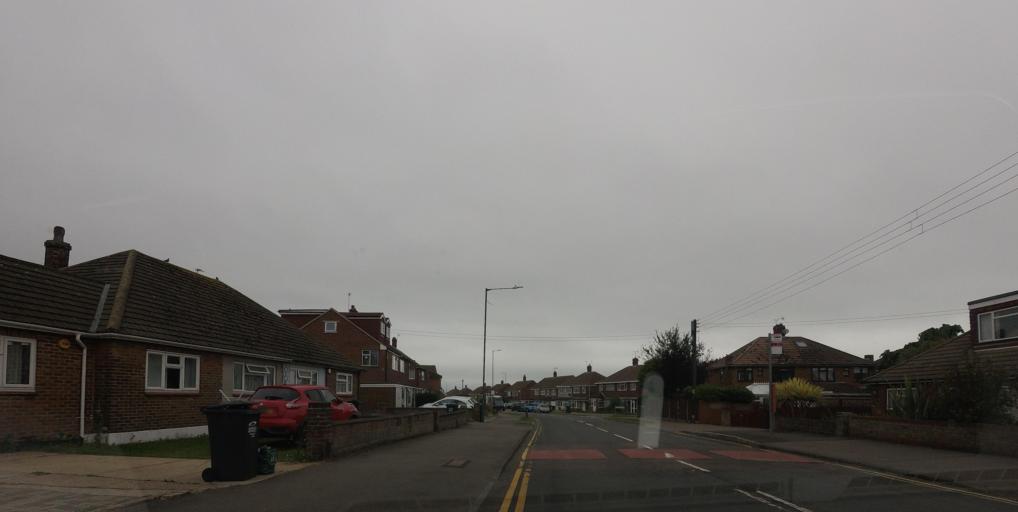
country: GB
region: England
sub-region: Kent
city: Stone
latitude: 51.4361
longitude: 0.2525
